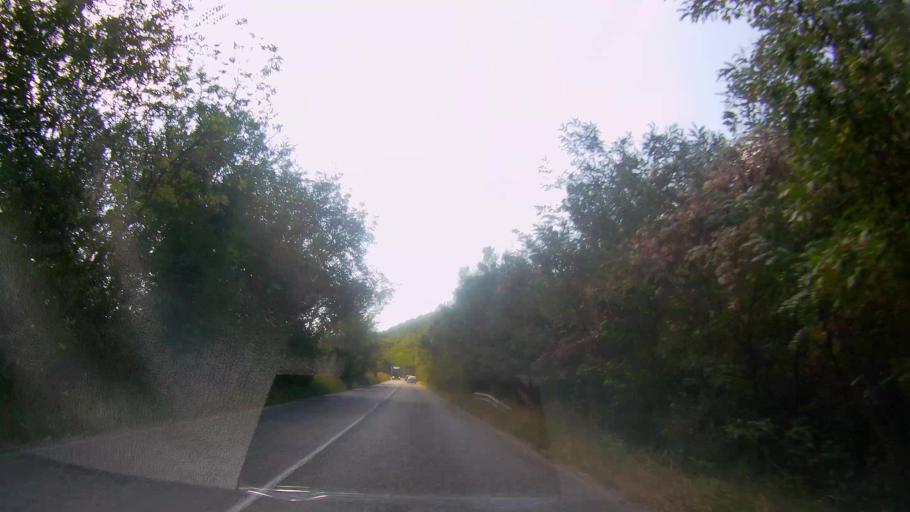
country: BG
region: Veliko Turnovo
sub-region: Obshtina Polski Trumbesh
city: Polski Trumbesh
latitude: 43.4387
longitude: 25.6542
